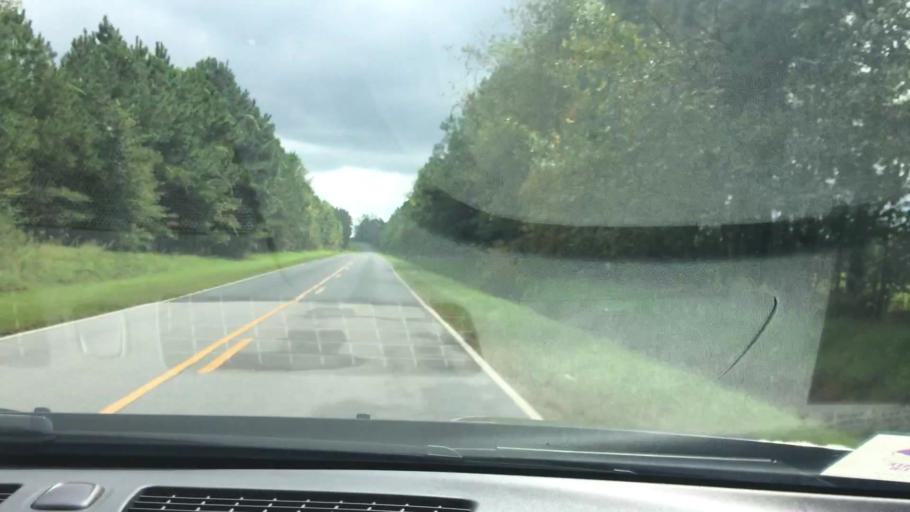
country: US
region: North Carolina
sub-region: Greene County
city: Maury
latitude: 35.5312
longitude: -77.5451
